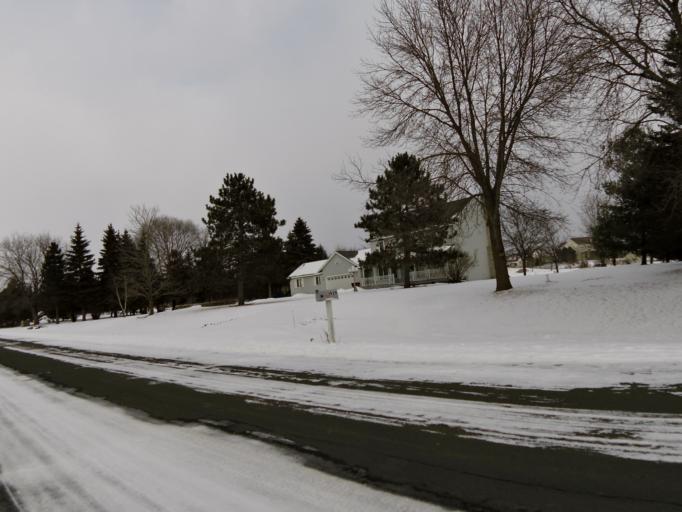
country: US
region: Minnesota
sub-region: Washington County
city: Lake Elmo
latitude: 44.9766
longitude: -92.8548
